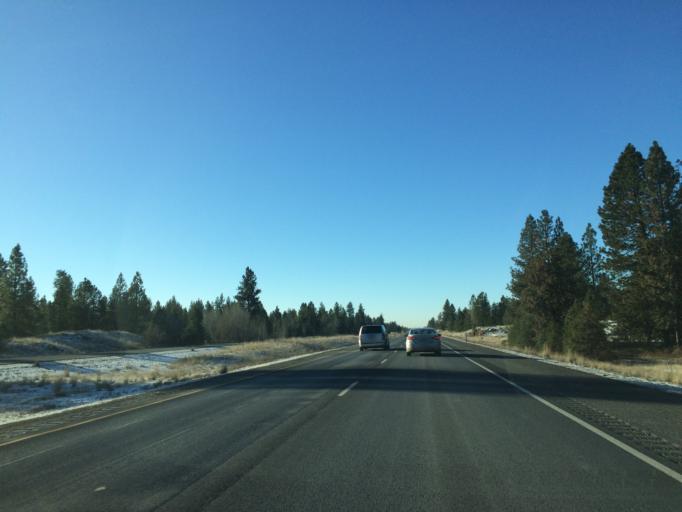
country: US
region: Washington
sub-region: Spokane County
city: Medical Lake
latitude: 47.4692
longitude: -117.7428
